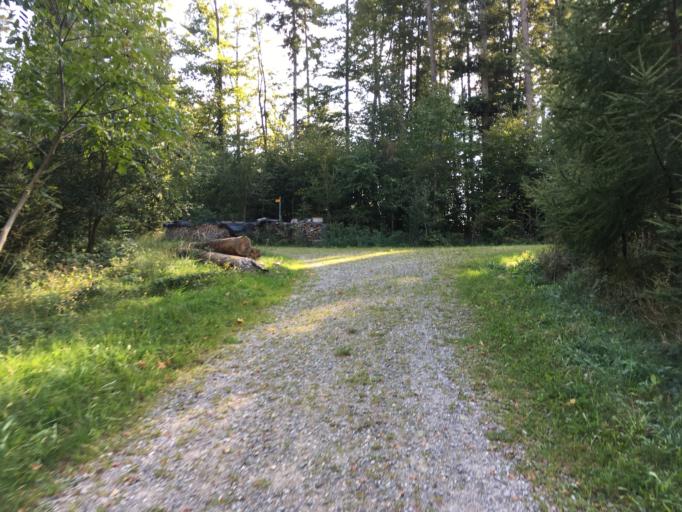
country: CH
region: Zurich
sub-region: Bezirk Hinwil
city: Wetzikon / Kempten
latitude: 47.3436
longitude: 8.8232
